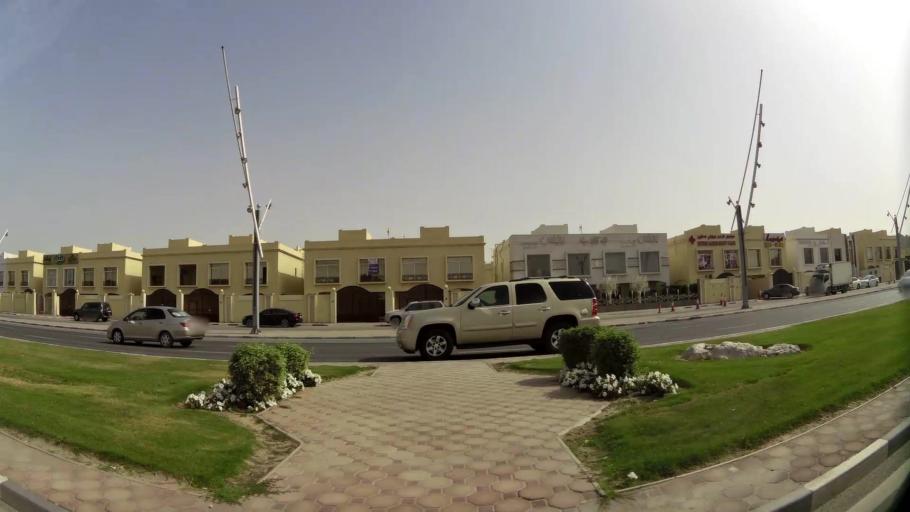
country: QA
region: Baladiyat ar Rayyan
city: Ar Rayyan
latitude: 25.2620
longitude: 51.4568
